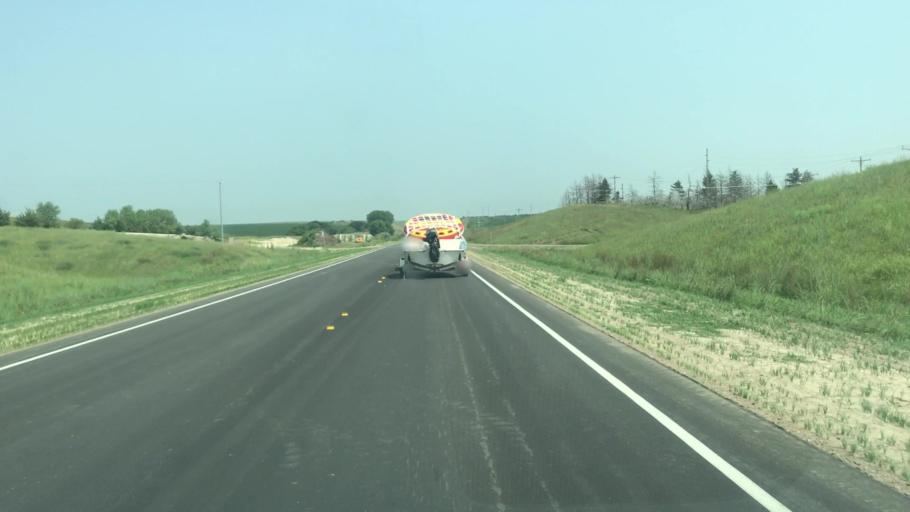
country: US
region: Nebraska
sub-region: Sherman County
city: Loup City
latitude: 41.2636
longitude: -98.9206
